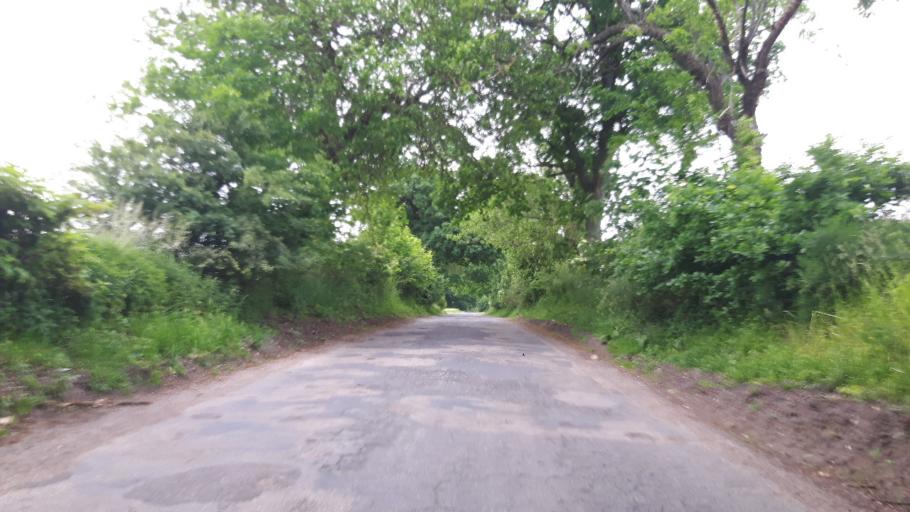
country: PL
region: West Pomeranian Voivodeship
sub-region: Powiat gryficki
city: Gryfice
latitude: 53.8484
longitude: 15.1608
